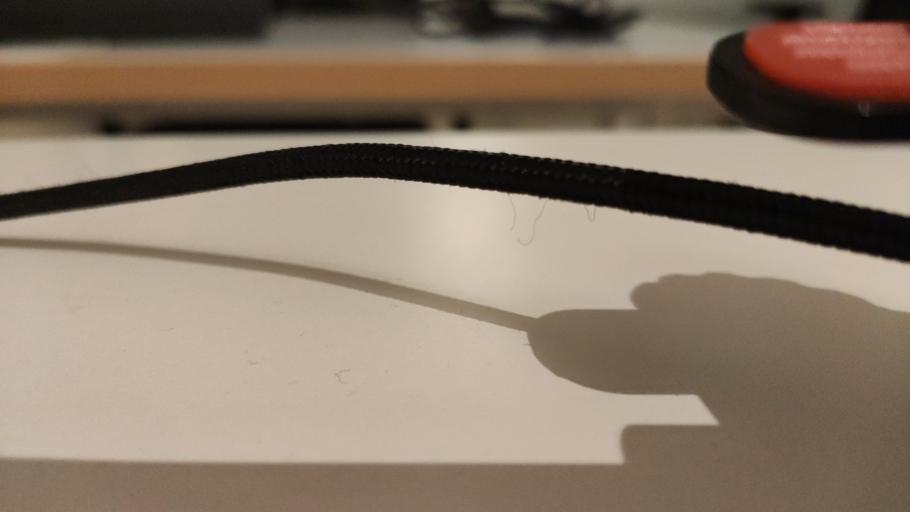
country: RU
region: Moskovskaya
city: Kabanovo
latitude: 55.7573
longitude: 38.9330
